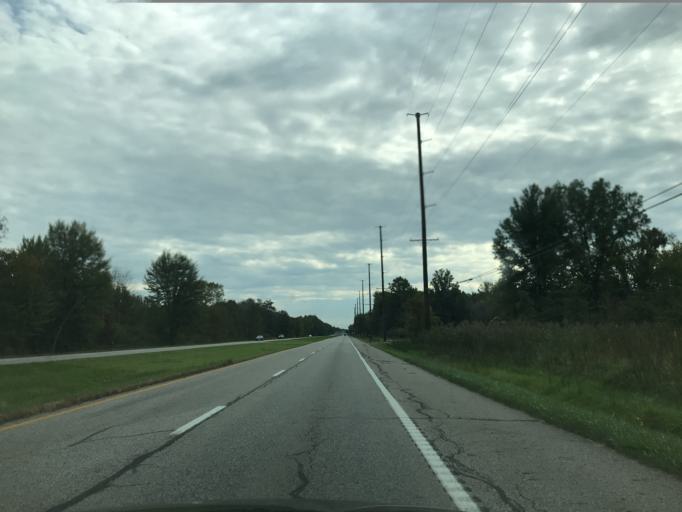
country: US
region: Ohio
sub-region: Trumbull County
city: Leavittsburg
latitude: 41.2735
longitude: -80.8986
